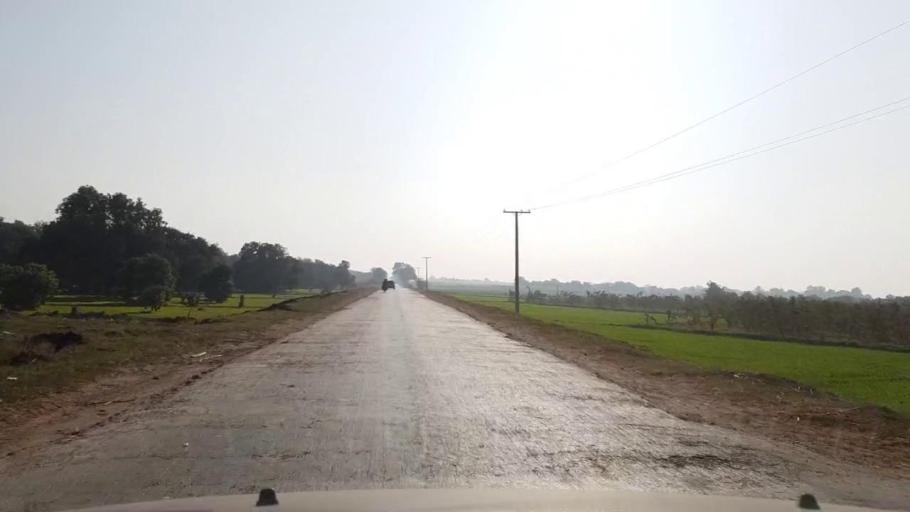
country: PK
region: Sindh
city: Matiari
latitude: 25.5617
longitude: 68.5266
